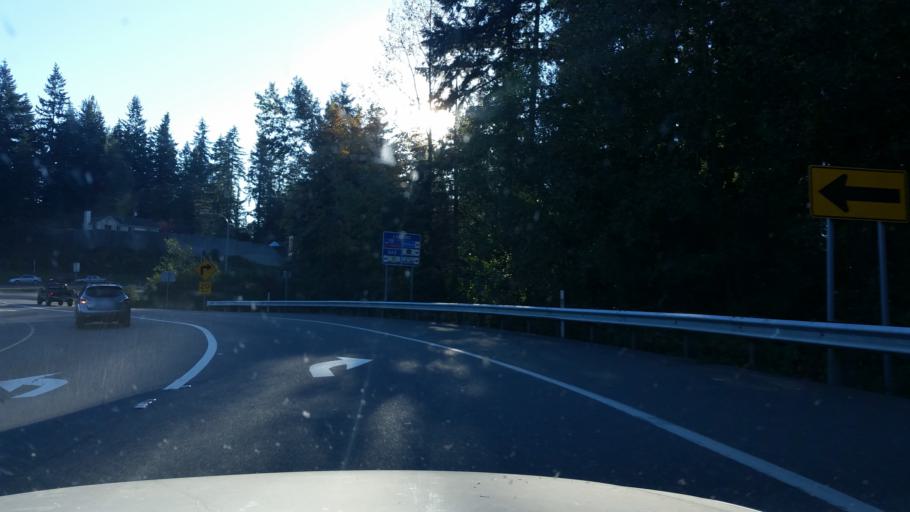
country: US
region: Washington
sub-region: Snohomish County
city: Mountlake Terrace
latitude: 47.7788
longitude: -122.3194
